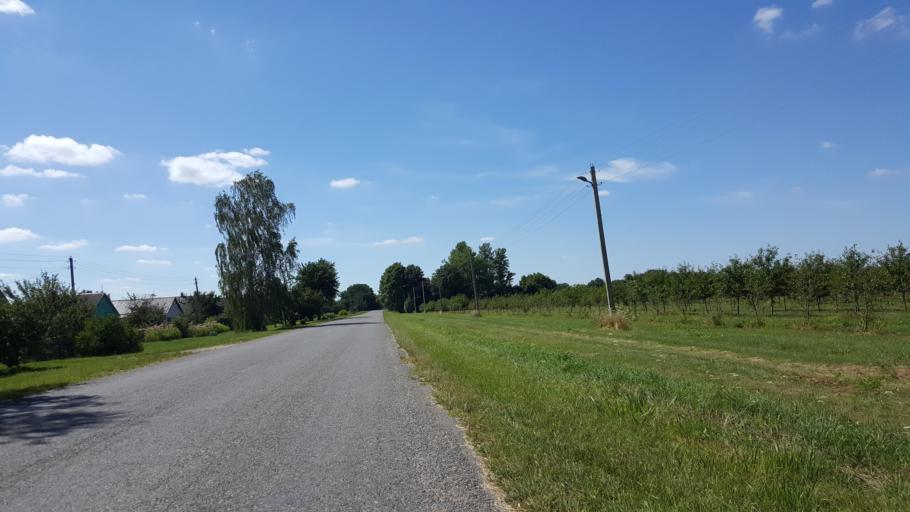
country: BY
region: Brest
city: Charnawchytsy
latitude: 52.3640
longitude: 23.6242
